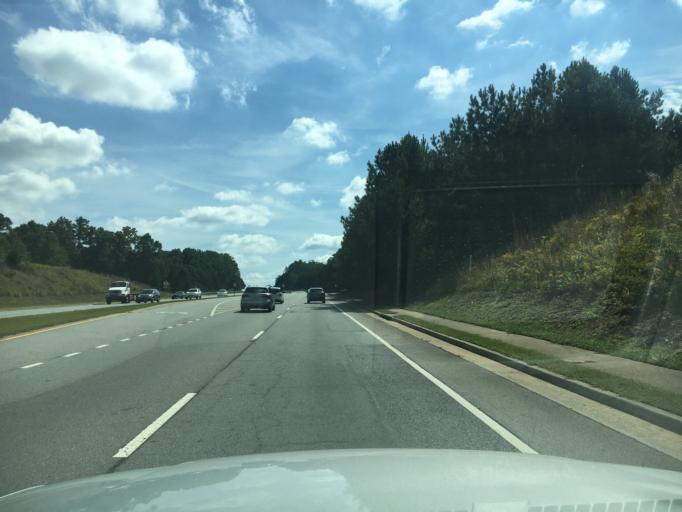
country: US
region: Georgia
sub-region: Gwinnett County
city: Duluth
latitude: 34.0189
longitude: -84.1165
